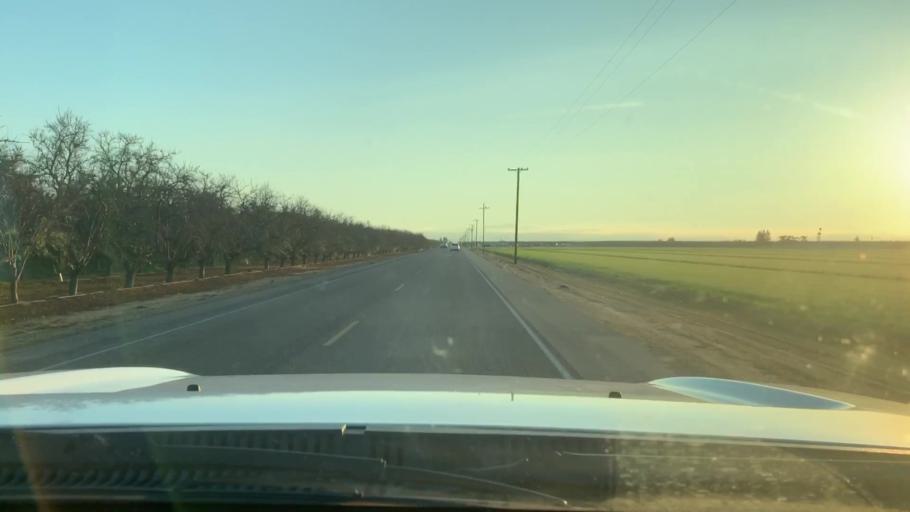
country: US
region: California
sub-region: Kern County
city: Shafter
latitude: 35.5001
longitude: -119.3582
